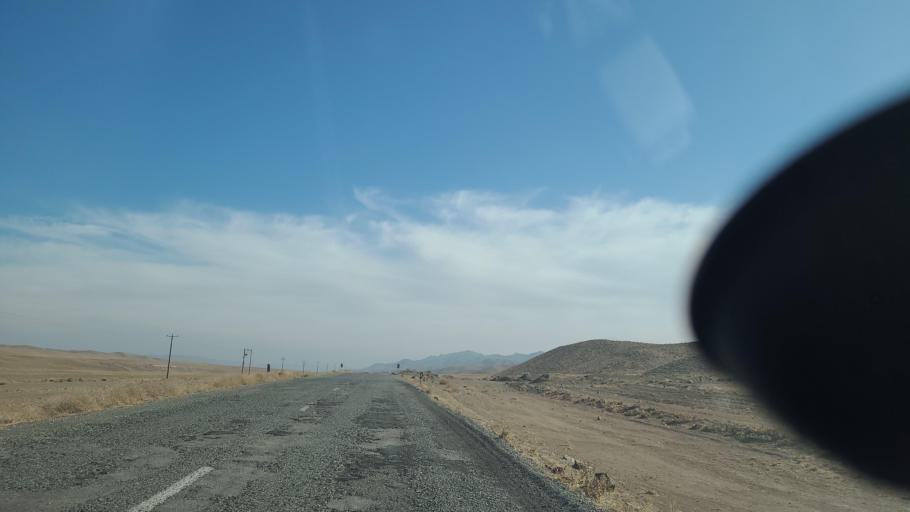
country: IR
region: Razavi Khorasan
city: Fariman
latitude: 35.5902
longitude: 59.6141
